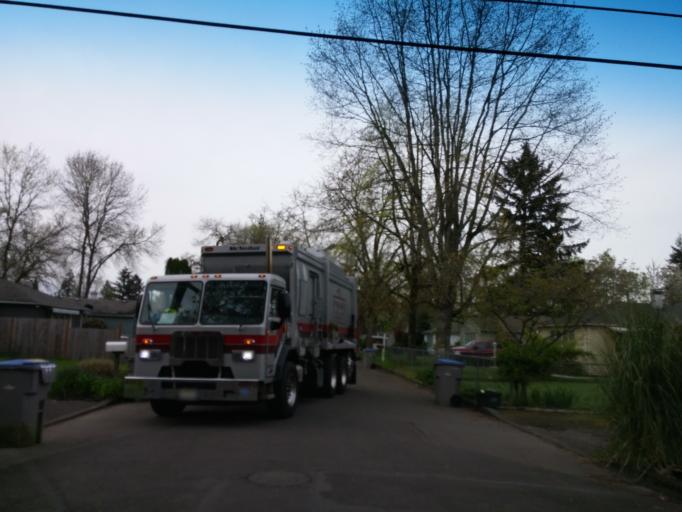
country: US
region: Oregon
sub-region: Washington County
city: Cedar Mill
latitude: 45.5174
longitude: -122.8137
